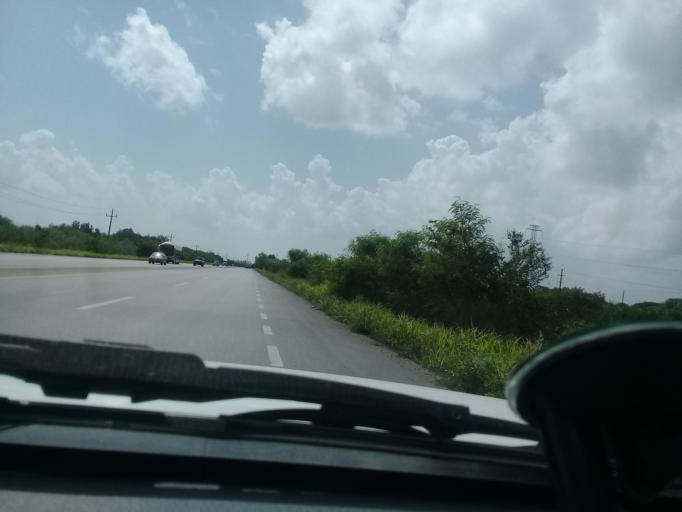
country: MX
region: Veracruz
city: Moralillo
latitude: 22.2132
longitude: -97.9723
